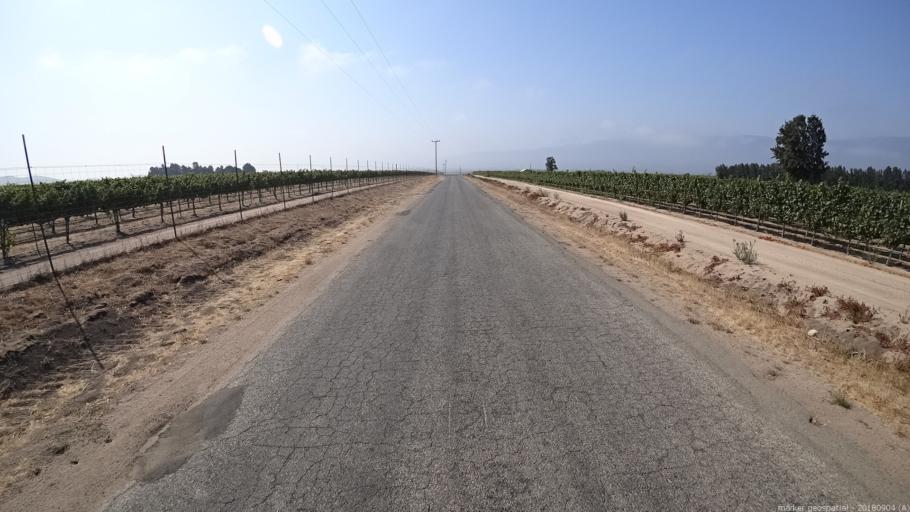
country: US
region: California
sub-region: Monterey County
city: Soledad
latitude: 36.4771
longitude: -121.3497
